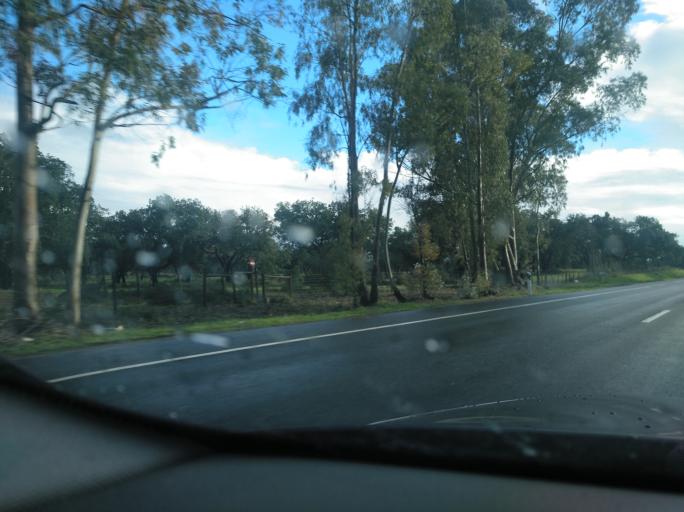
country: PT
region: Setubal
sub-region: Grandola
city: Grandola
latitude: 38.0293
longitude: -8.3999
